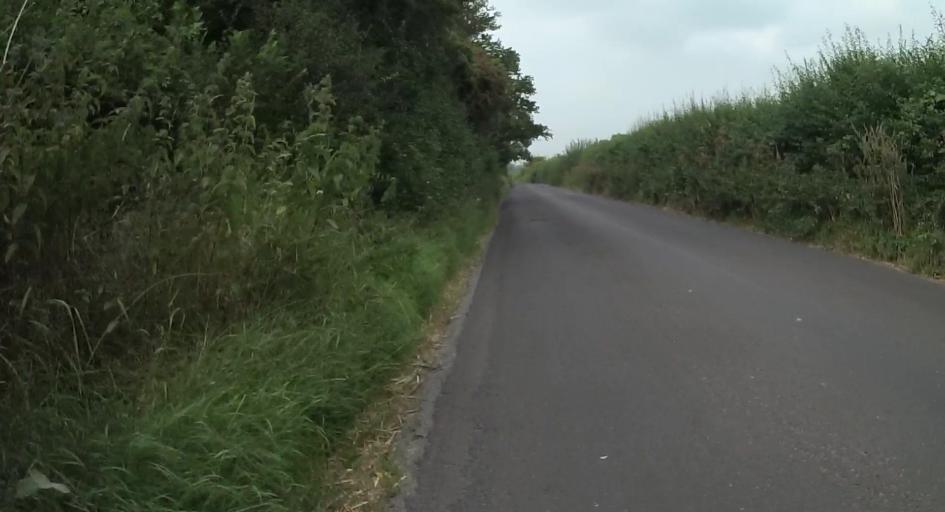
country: GB
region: England
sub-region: Hampshire
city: Old Basing
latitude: 51.2497
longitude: -1.0429
